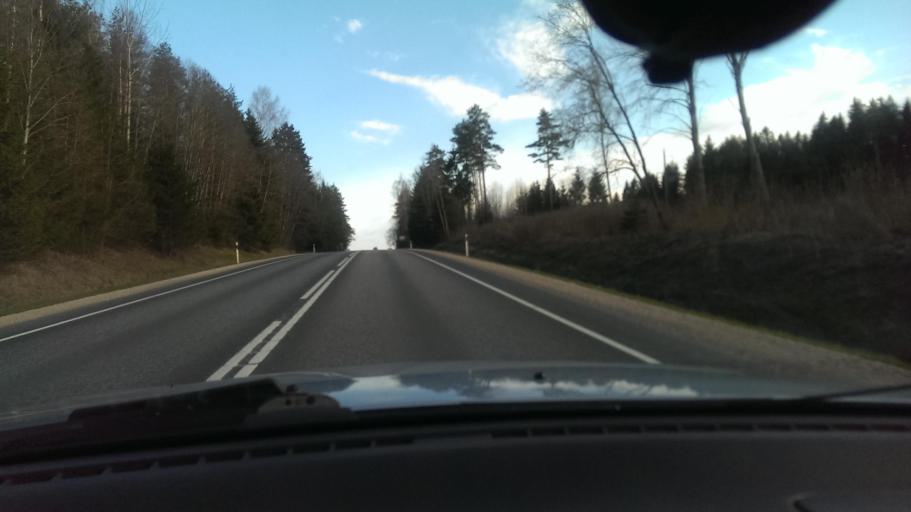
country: EE
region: Vorumaa
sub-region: Antsla vald
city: Vana-Antsla
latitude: 58.0002
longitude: 26.7618
